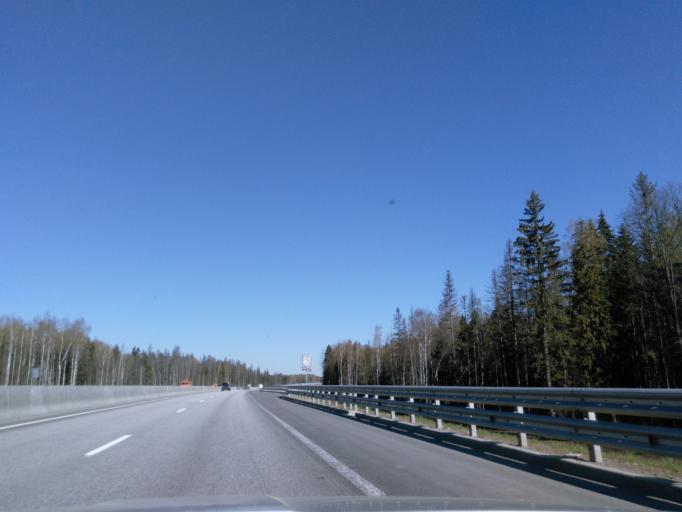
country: RU
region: Moskovskaya
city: Mendeleyevo
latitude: 56.0723
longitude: 37.2184
